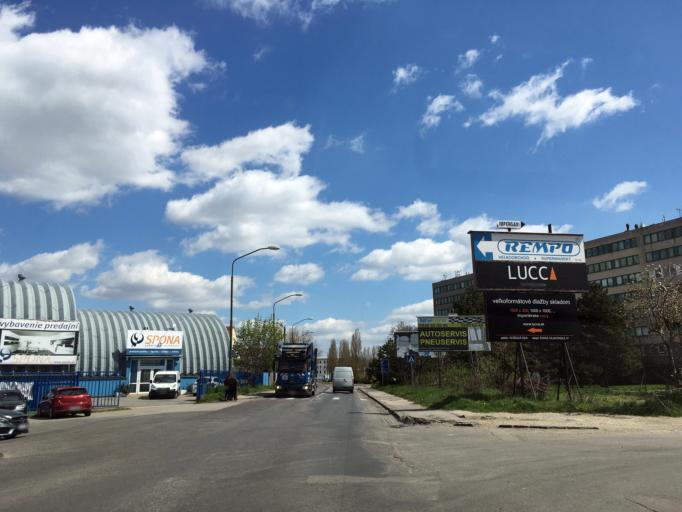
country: SK
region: Bratislavsky
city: Bratislava
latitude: 48.1874
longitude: 17.1682
